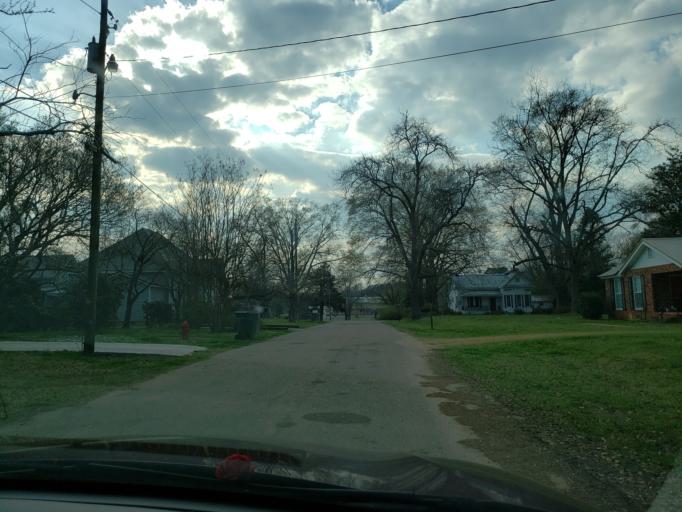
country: US
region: Alabama
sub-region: Hale County
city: Greensboro
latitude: 32.7017
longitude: -87.6047
